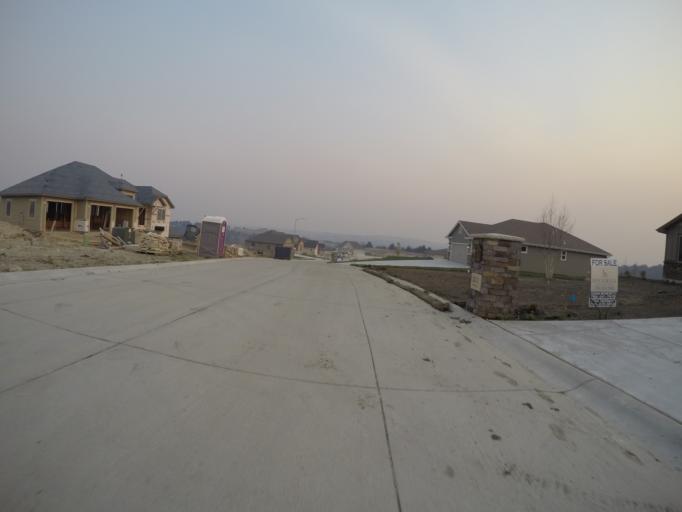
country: US
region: Kansas
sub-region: Riley County
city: Manhattan
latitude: 39.2059
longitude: -96.6534
